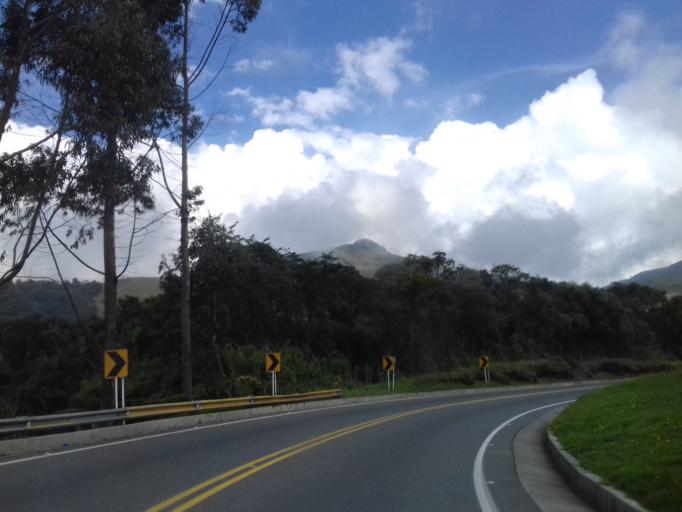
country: CO
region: Caldas
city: Villamaria
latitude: 5.0216
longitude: -75.3661
